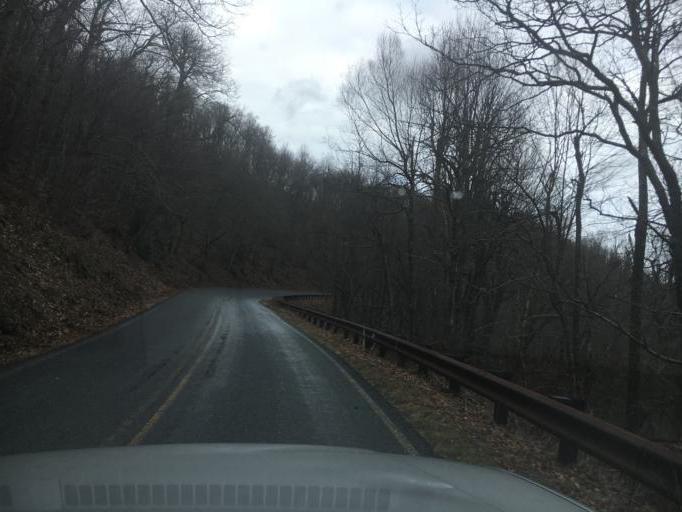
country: US
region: North Carolina
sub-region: Transylvania County
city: Brevard
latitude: 35.3682
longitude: -82.7897
